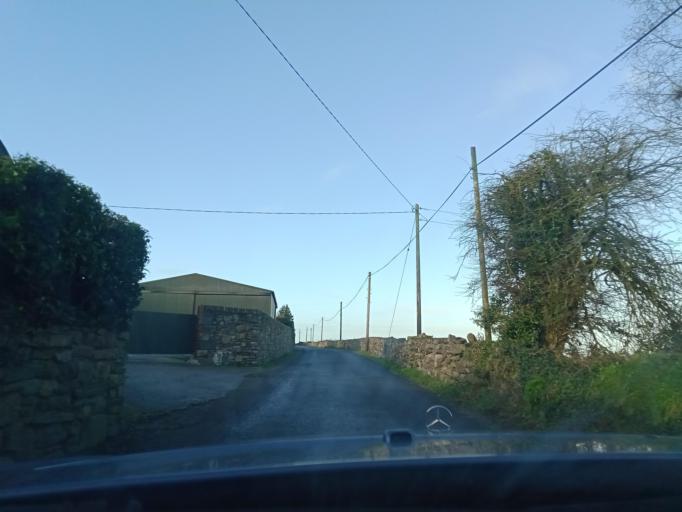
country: IE
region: Leinster
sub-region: Kilkenny
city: Callan
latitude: 52.4708
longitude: -7.4177
